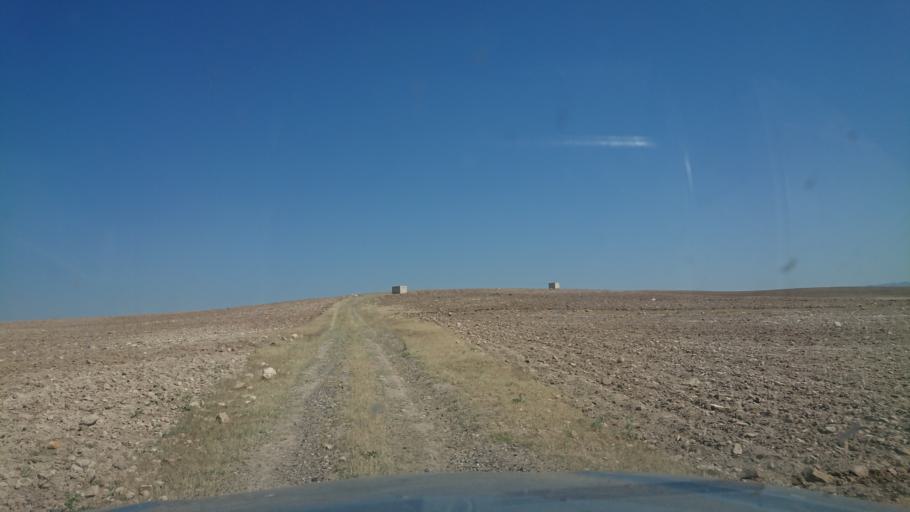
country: TR
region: Aksaray
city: Sariyahsi
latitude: 39.0511
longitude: 33.8891
